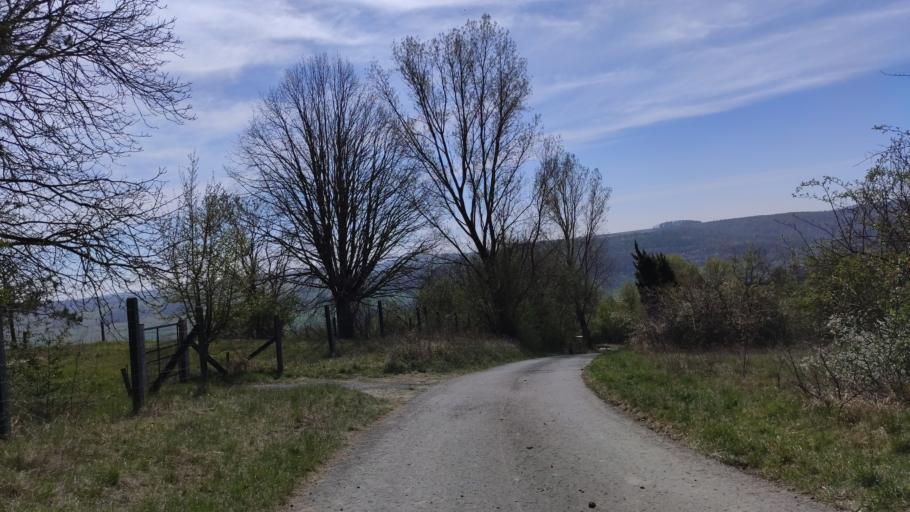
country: DE
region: Lower Saxony
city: Boffzen
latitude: 51.7190
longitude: 9.3001
